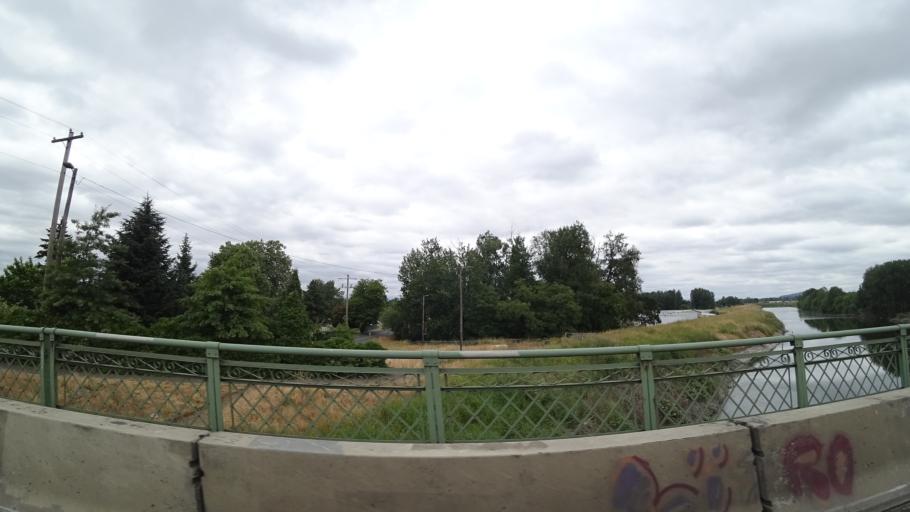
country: US
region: Washington
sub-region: Clark County
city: Vancouver
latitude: 45.5867
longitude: -122.6642
